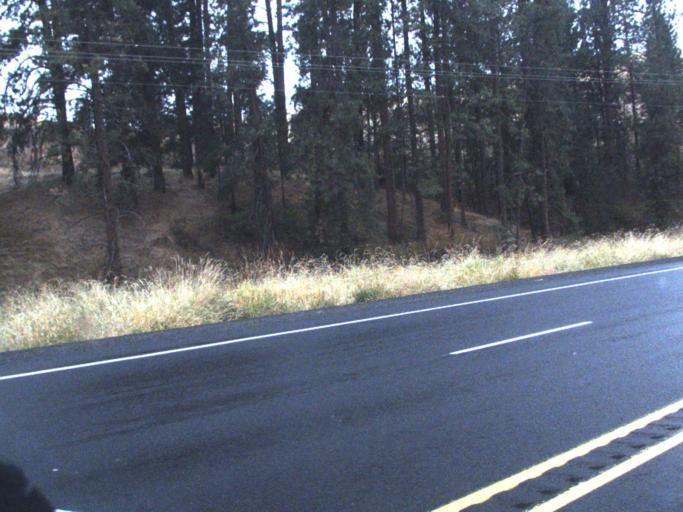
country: US
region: Washington
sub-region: Whitman County
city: Colfax
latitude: 46.8650
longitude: -117.3569
